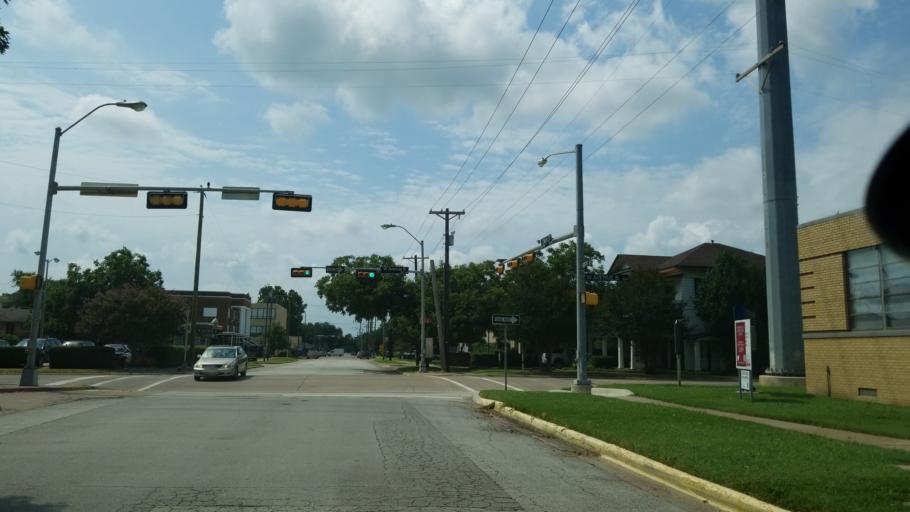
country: US
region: Texas
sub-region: Dallas County
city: Garland
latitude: 32.9112
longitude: -96.6415
